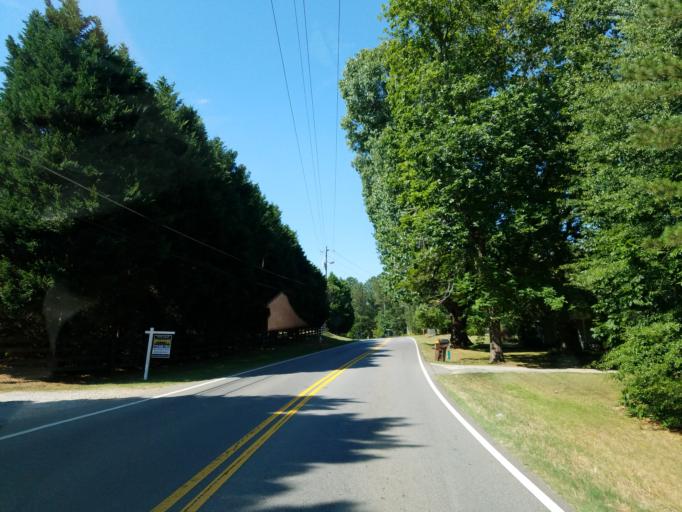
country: US
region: Georgia
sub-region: Fulton County
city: Milton
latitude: 34.1383
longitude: -84.3440
